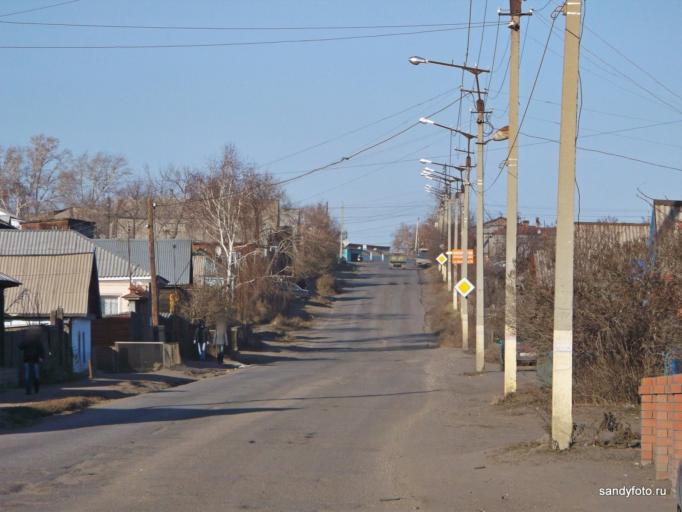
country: RU
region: Chelyabinsk
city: Troitsk
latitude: 54.0981
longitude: 61.5881
